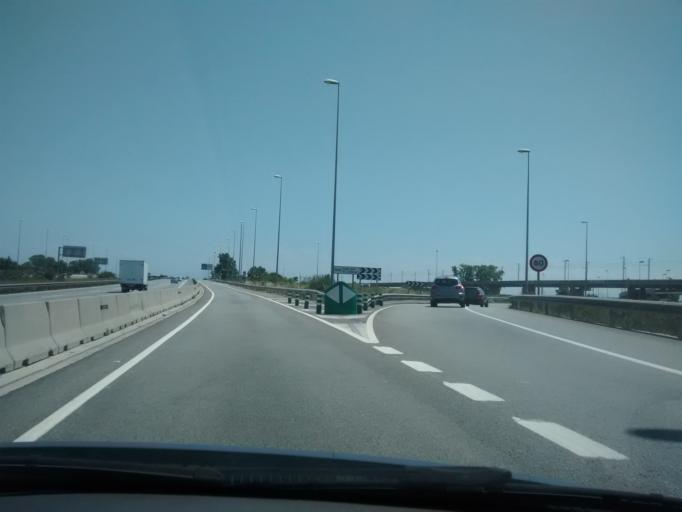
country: ES
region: Catalonia
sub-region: Provincia de Barcelona
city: Sant Joan Despi
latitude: 41.3546
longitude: 2.0536
